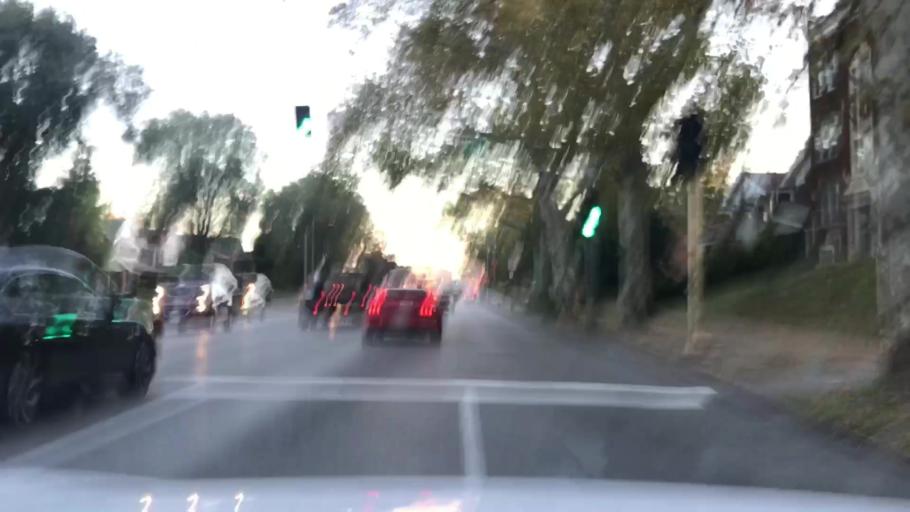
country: US
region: Missouri
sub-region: Saint Louis County
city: Richmond Heights
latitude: 38.6101
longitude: -90.2681
